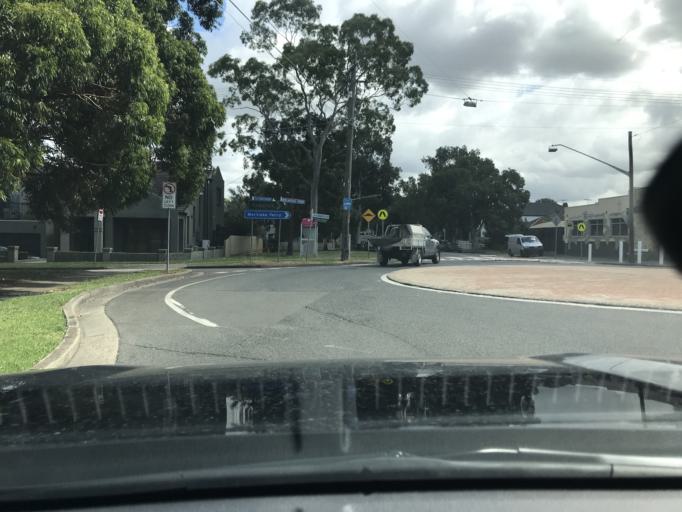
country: AU
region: New South Wales
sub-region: Canada Bay
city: Concord
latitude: -33.8521
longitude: 151.1075
